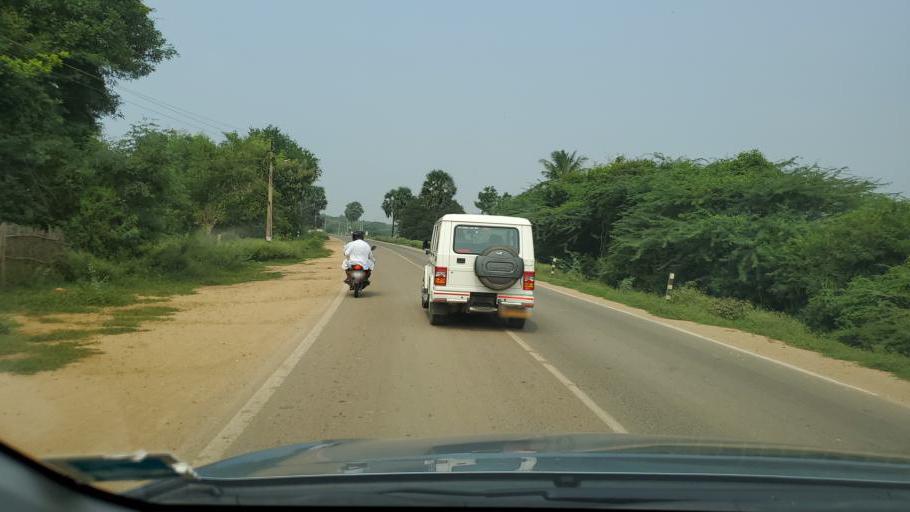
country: IN
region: Tamil Nadu
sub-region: Ariyalur
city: Ariyalur
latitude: 11.1226
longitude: 79.1445
